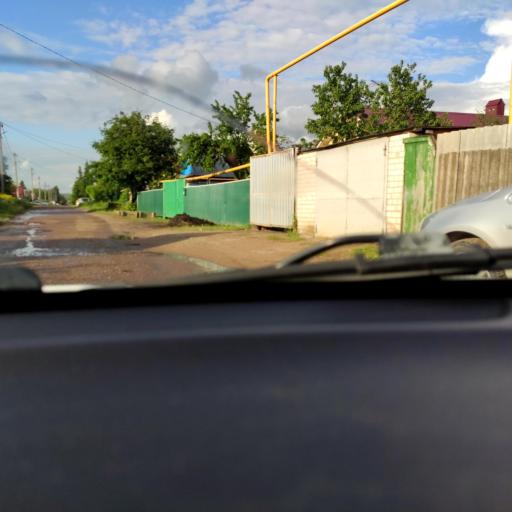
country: RU
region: Tatarstan
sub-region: Gorod Kazan'
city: Kazan
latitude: 55.8534
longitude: 49.1892
